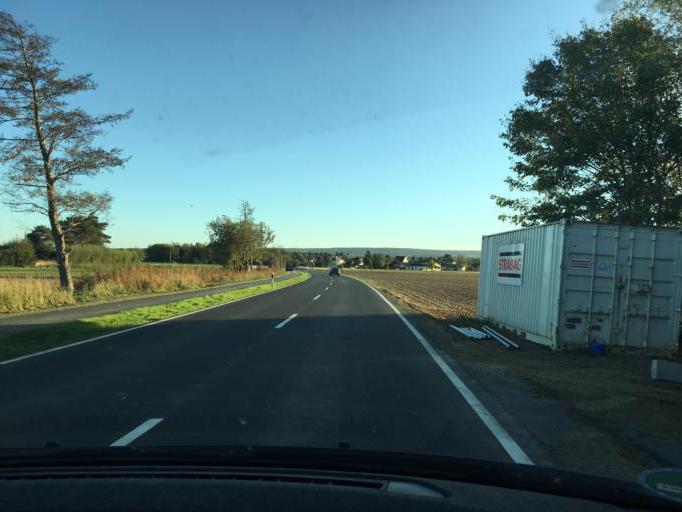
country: DE
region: North Rhine-Westphalia
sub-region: Regierungsbezirk Koln
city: Langerwehe
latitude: 50.8073
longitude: 6.3957
